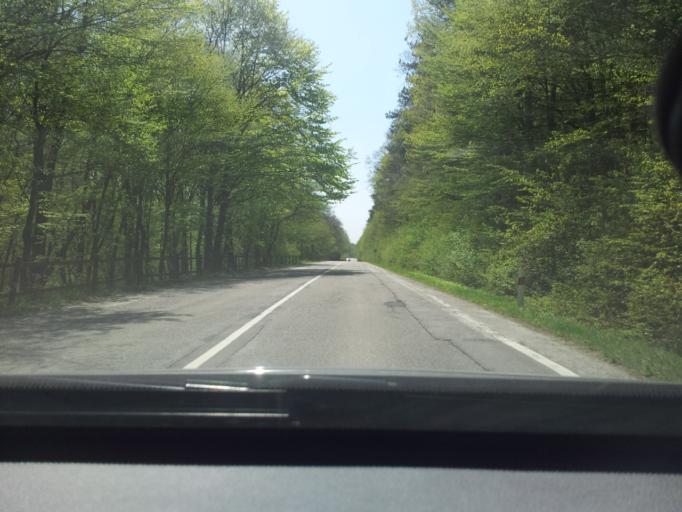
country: SK
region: Nitriansky
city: Zlate Moravce
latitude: 48.4724
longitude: 18.4108
